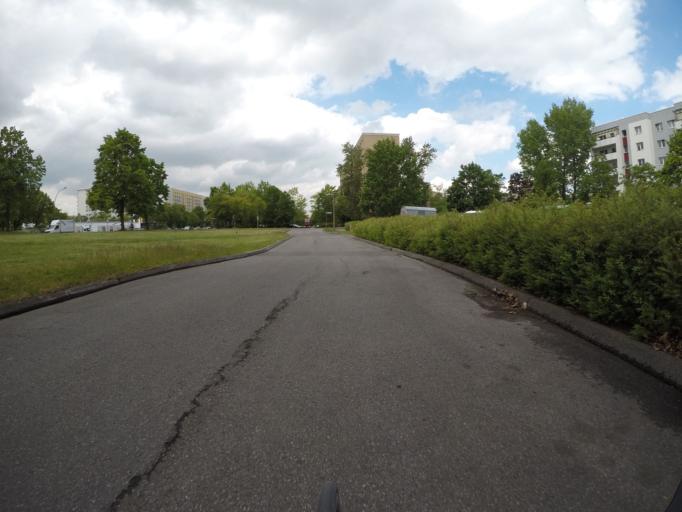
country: DE
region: Berlin
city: Marzahn
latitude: 52.5492
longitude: 13.5547
